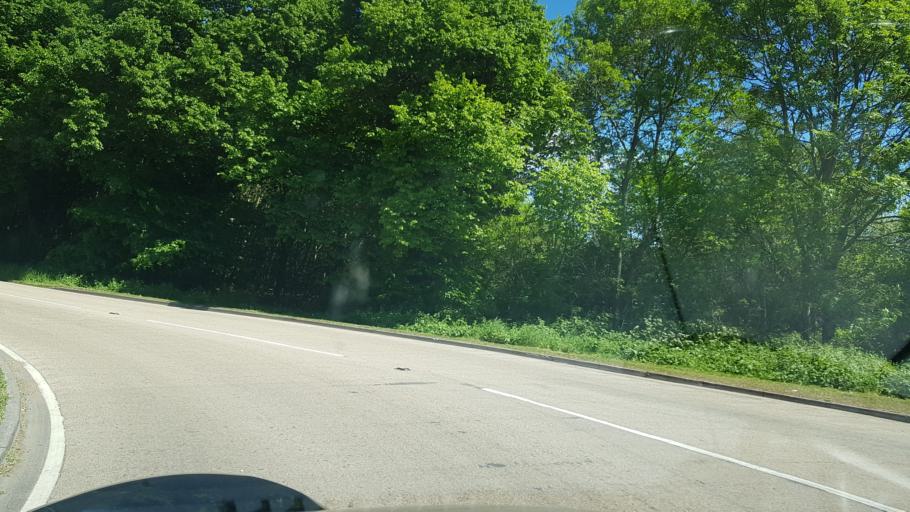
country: GB
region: England
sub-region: Surrey
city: Cranleigh
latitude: 51.1331
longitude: -0.5378
